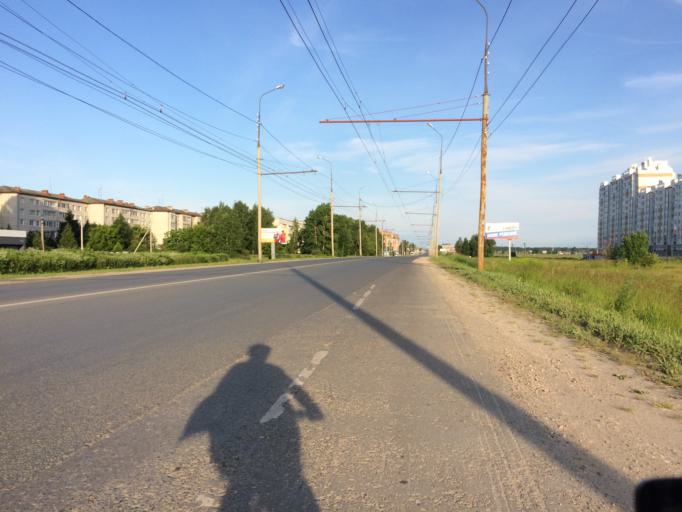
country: RU
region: Mariy-El
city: Medvedevo
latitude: 56.6387
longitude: 47.8091
